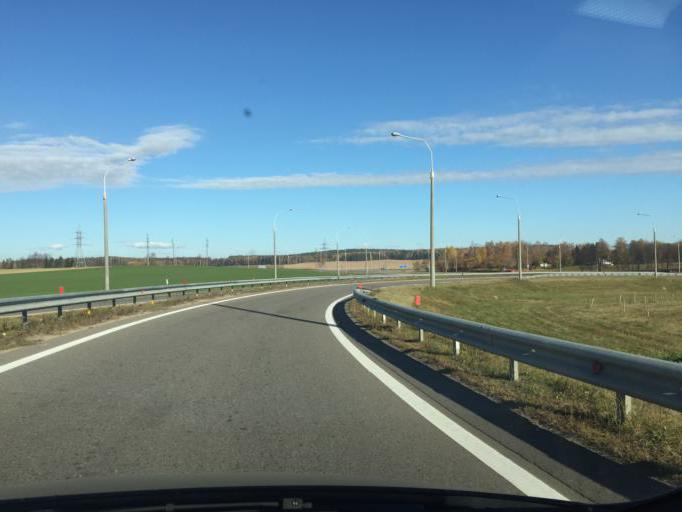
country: BY
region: Minsk
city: Slabada
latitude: 54.0167
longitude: 27.8865
